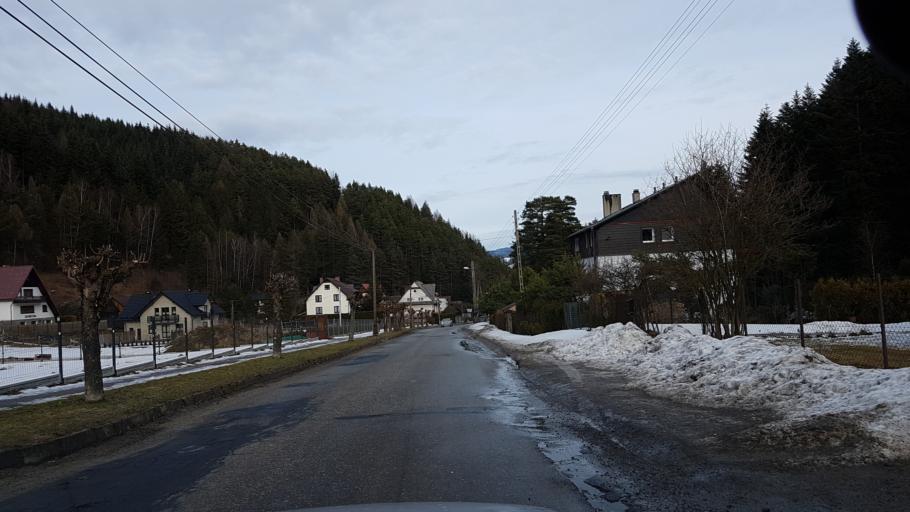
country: PL
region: Lesser Poland Voivodeship
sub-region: Powiat nowosadecki
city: Piwniczna-Zdroj
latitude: 49.4292
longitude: 20.6685
